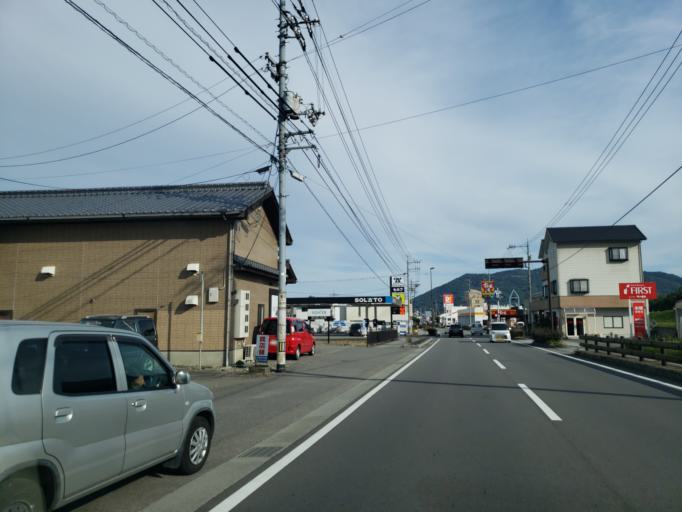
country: JP
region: Tokushima
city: Wakimachi
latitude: 34.0648
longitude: 134.1521
